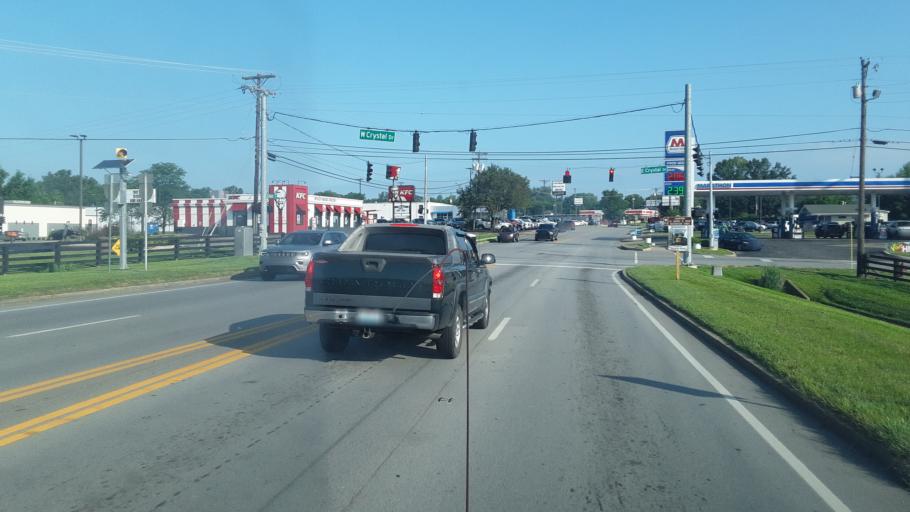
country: US
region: Kentucky
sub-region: Oldham County
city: La Grange
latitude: 38.4011
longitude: -85.3755
